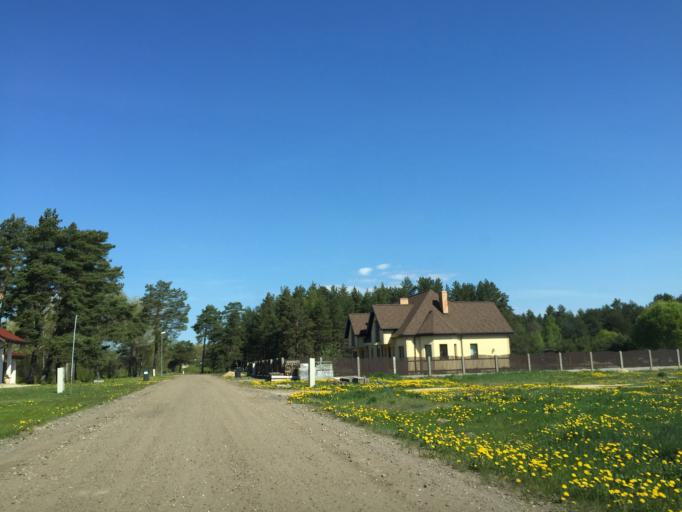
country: LV
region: Adazi
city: Adazi
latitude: 57.0987
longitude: 24.3401
